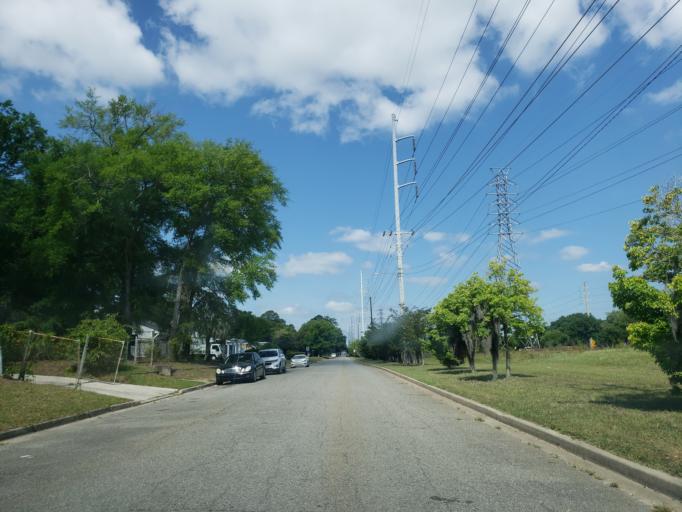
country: US
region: Georgia
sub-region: Chatham County
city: Thunderbolt
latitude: 32.0678
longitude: -81.0512
